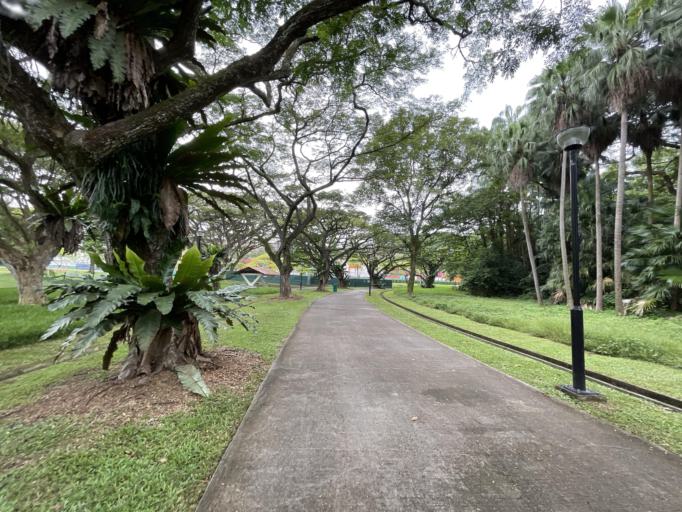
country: SG
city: Singapore
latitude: 1.2876
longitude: 103.7742
